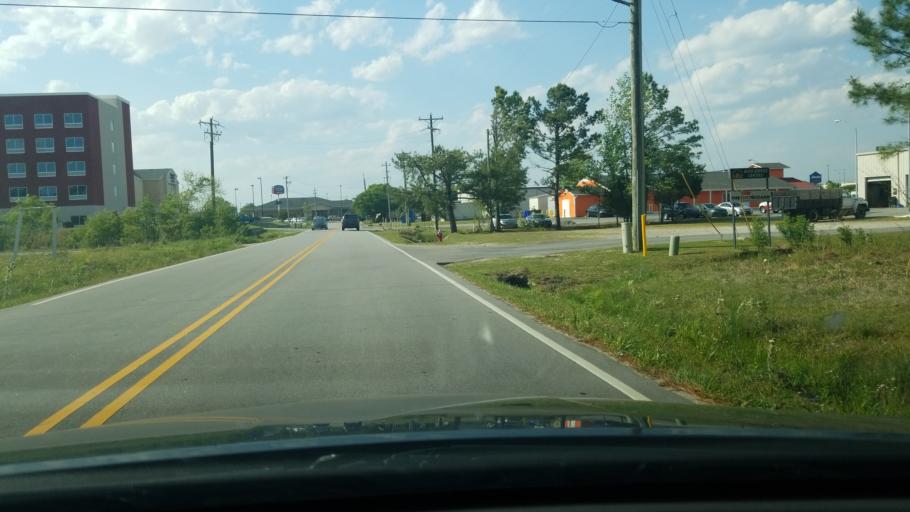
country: US
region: North Carolina
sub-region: Onslow County
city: Pumpkin Center
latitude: 34.7801
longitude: -77.3973
